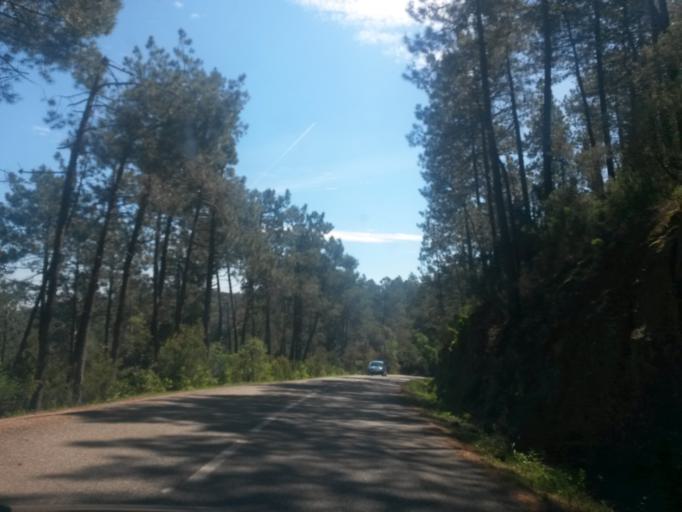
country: ES
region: Catalonia
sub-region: Provincia de Girona
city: Madremanya
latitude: 41.9827
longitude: 2.9429
